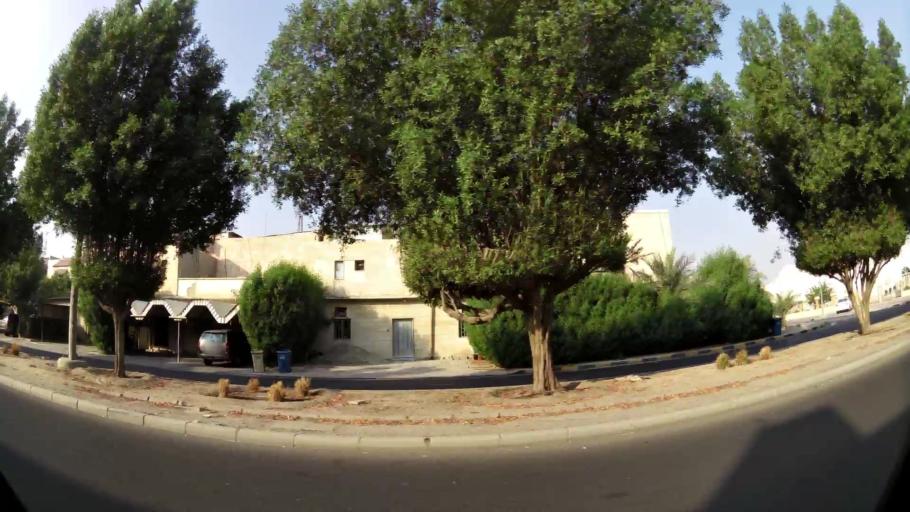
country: KW
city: Bayan
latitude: 29.2914
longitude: 48.0562
